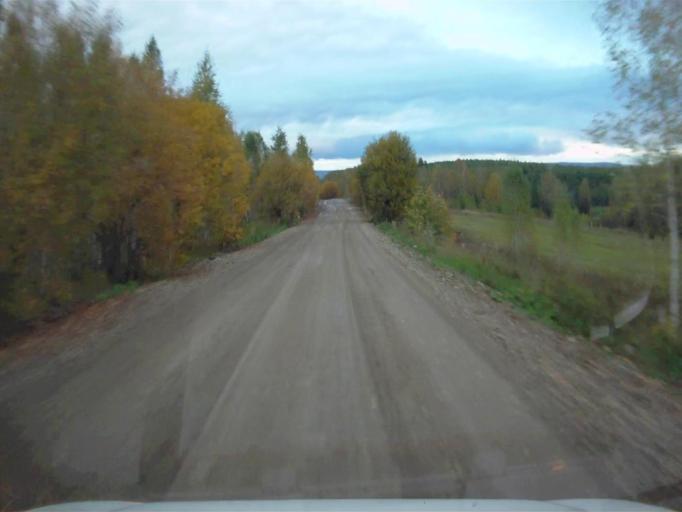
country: RU
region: Sverdlovsk
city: Mikhaylovsk
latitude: 56.2076
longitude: 59.2069
